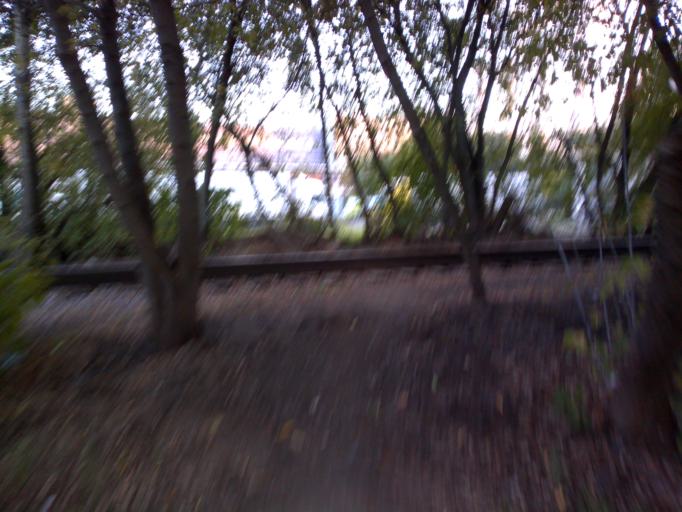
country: RU
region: Moscow
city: Zagor'ye
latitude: 55.5903
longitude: 37.6636
